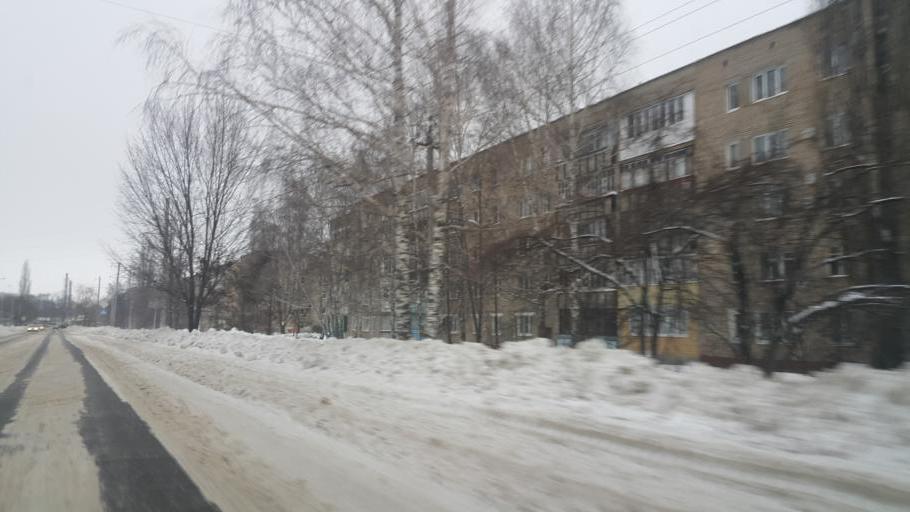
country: RU
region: Tambov
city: Bokino
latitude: 52.6501
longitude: 41.4513
